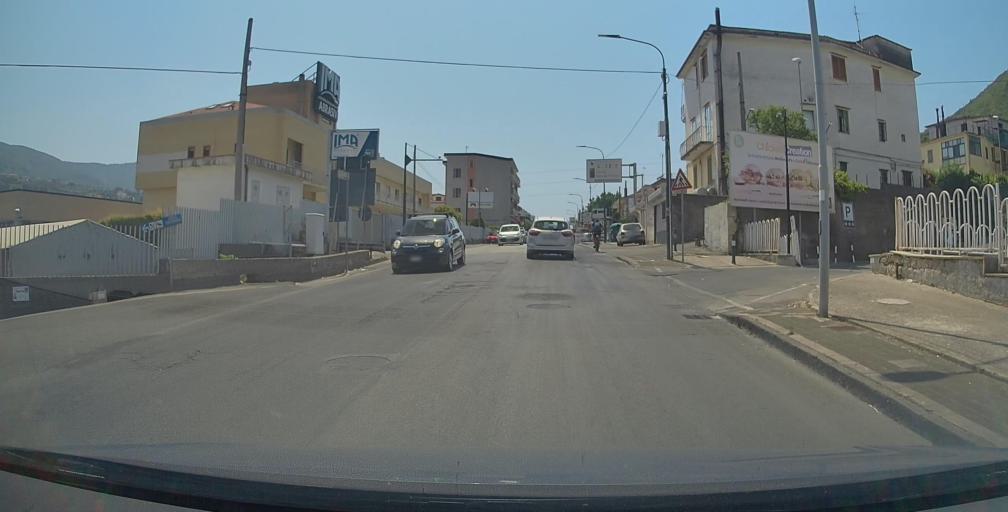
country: IT
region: Campania
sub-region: Provincia di Salerno
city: Nocera Superiore
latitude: 40.7283
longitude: 14.6903
